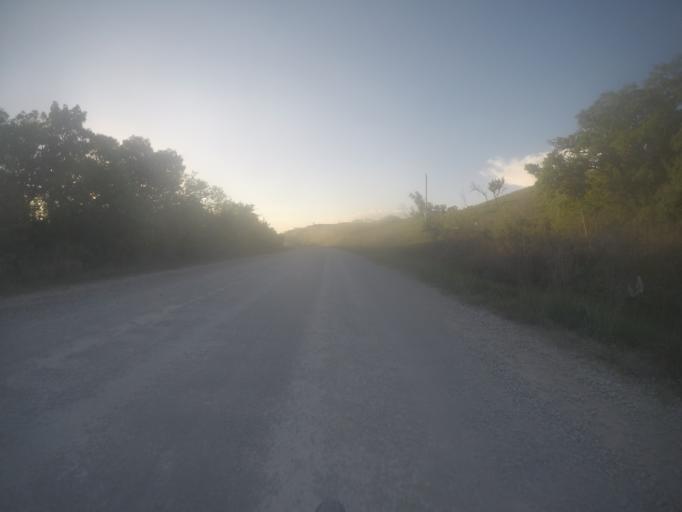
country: US
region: Kansas
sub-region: Riley County
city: Manhattan
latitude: 39.2390
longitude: -96.5582
